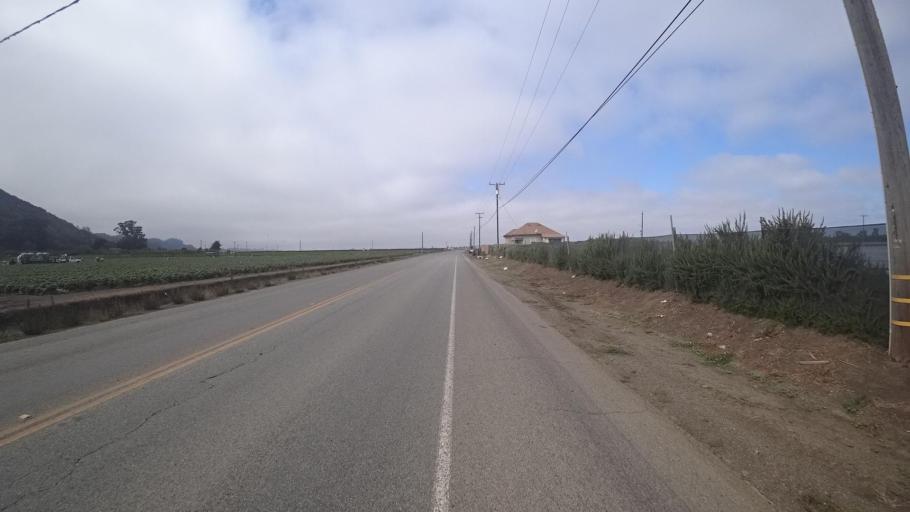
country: US
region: California
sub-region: Monterey County
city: Pajaro
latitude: 36.9035
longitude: -121.7093
